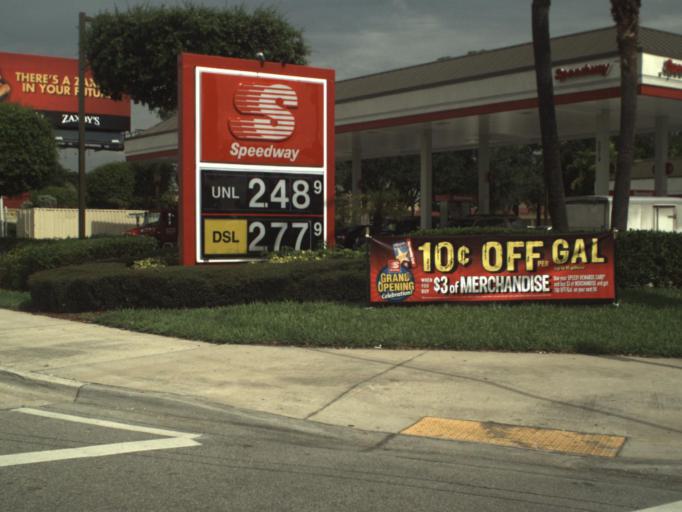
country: US
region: Florida
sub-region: Palm Beach County
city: Schall Circle
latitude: 26.7072
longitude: -80.1195
